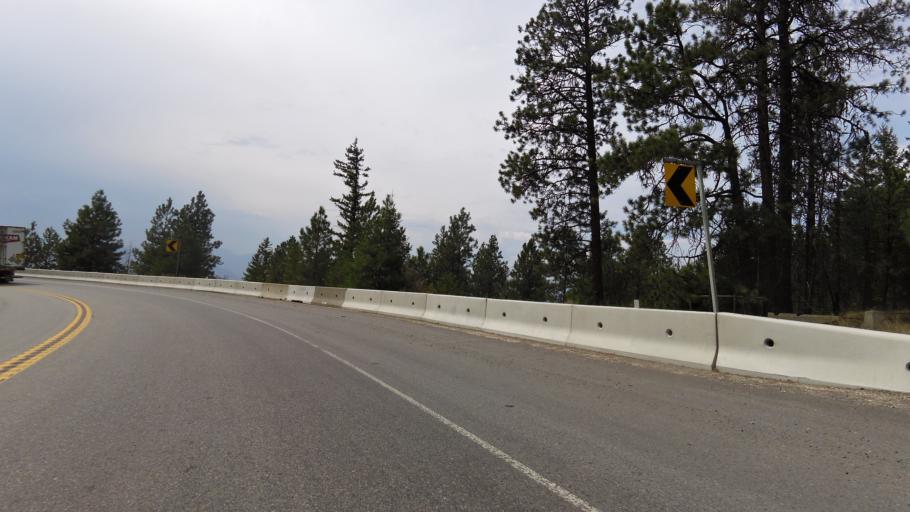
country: CA
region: British Columbia
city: Osoyoos
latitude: 49.0209
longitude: -119.3673
